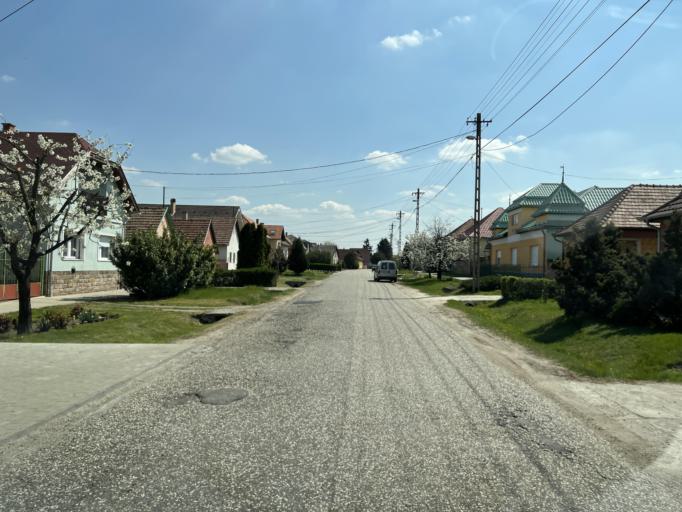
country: HU
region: Pest
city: Orbottyan
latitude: 47.6595
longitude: 19.2328
